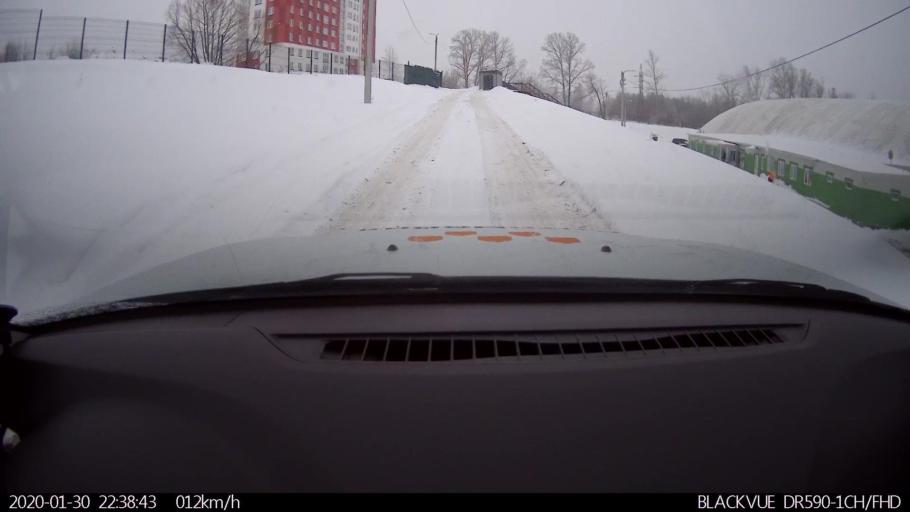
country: RU
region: Nizjnij Novgorod
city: Nizhniy Novgorod
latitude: 56.2927
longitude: 43.9758
